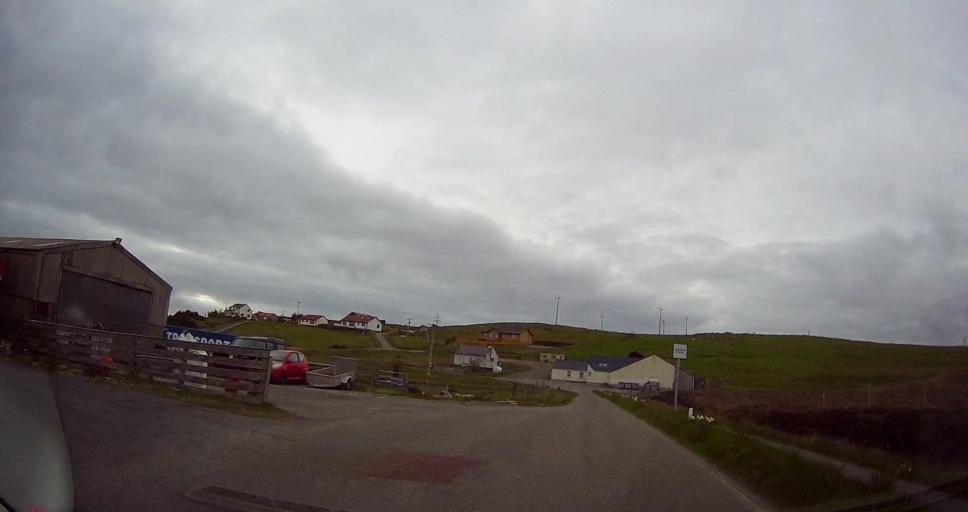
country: GB
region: Scotland
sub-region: Shetland Islands
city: Shetland
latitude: 60.5009
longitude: -1.0622
